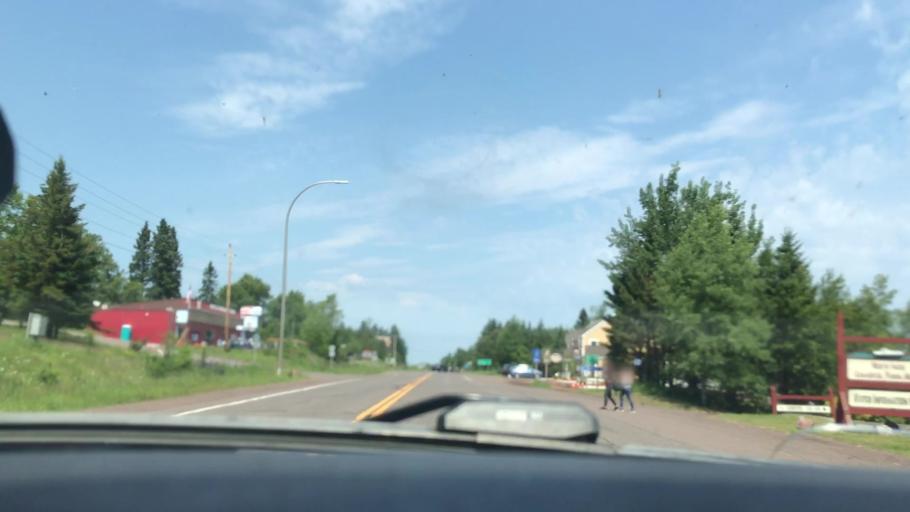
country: US
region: Minnesota
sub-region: Lake County
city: Silver Bay
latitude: 47.5762
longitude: -90.8318
